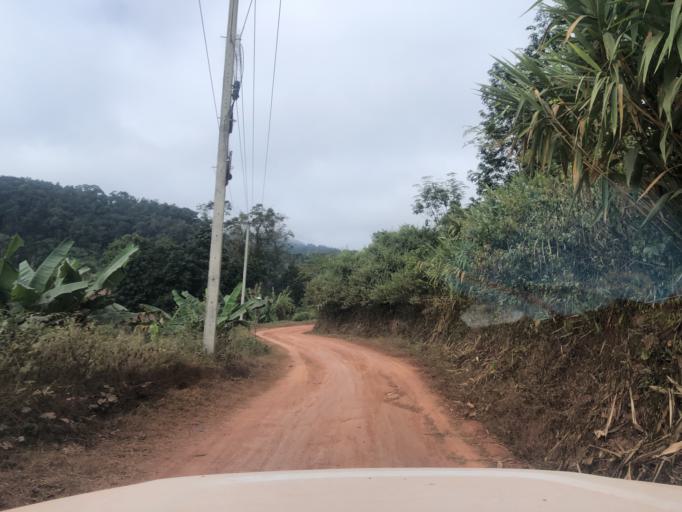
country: LA
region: Phongsali
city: Phongsali
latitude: 21.3115
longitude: 101.9650
